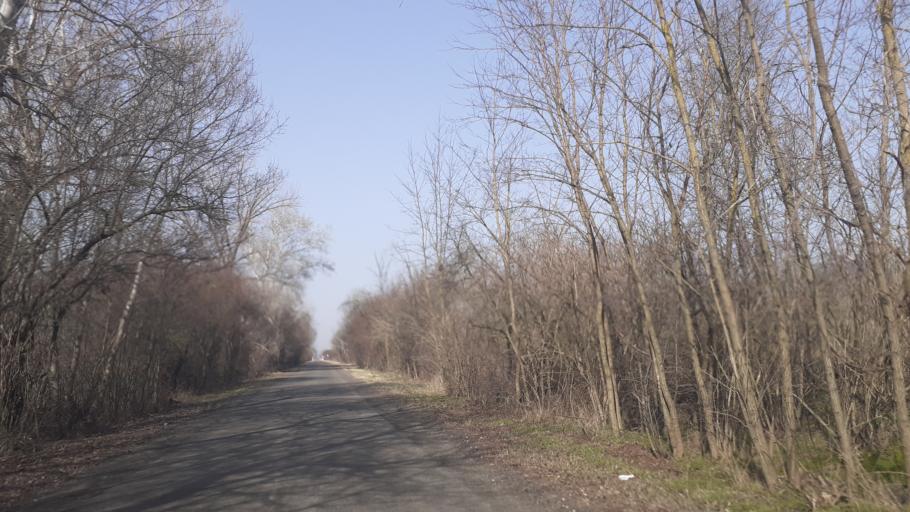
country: HU
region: Pest
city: Dabas
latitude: 47.1116
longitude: 19.2210
